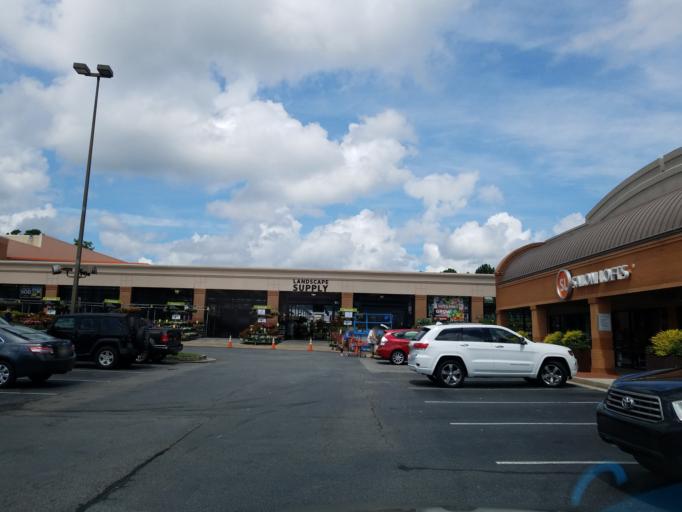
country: US
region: Georgia
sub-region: Fulton County
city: Sandy Springs
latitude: 33.9814
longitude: -84.4343
